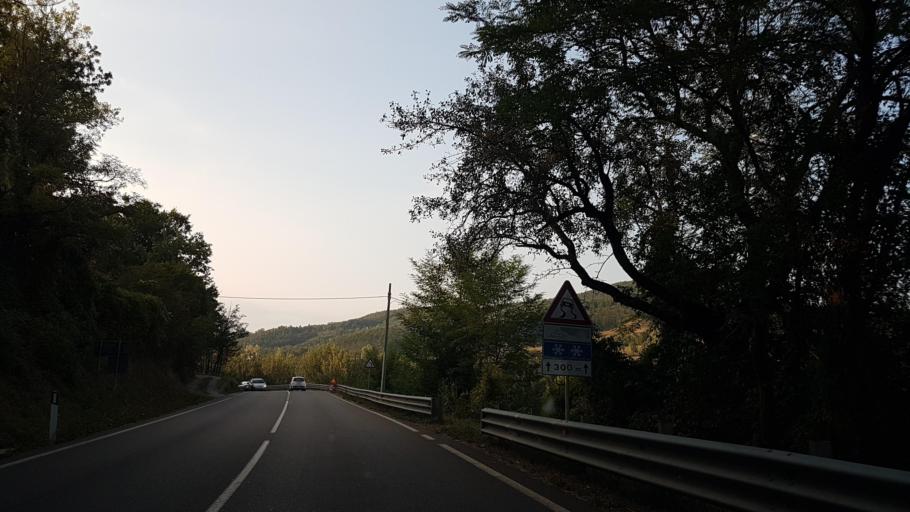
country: IT
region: Emilia-Romagna
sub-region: Provincia di Parma
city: Albareto
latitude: 44.4696
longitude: 9.7301
